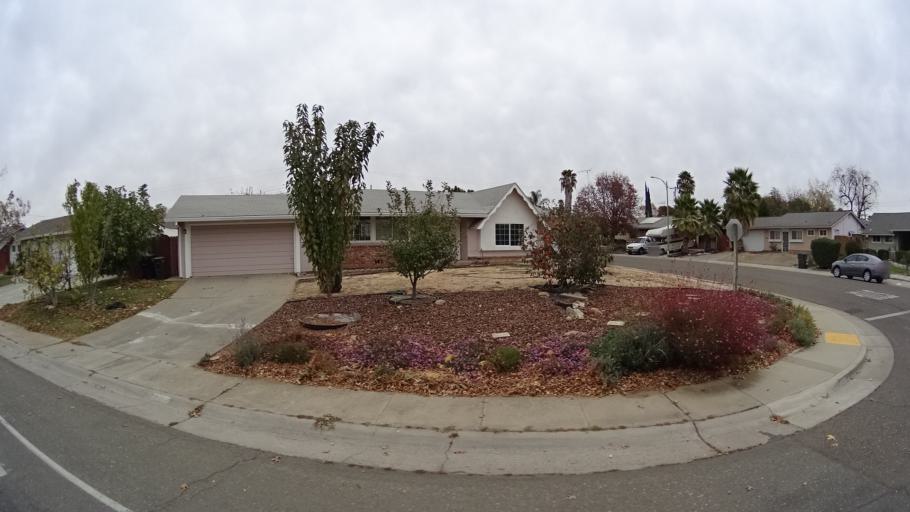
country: US
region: California
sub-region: Sacramento County
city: Citrus Heights
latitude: 38.6982
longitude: -121.2984
